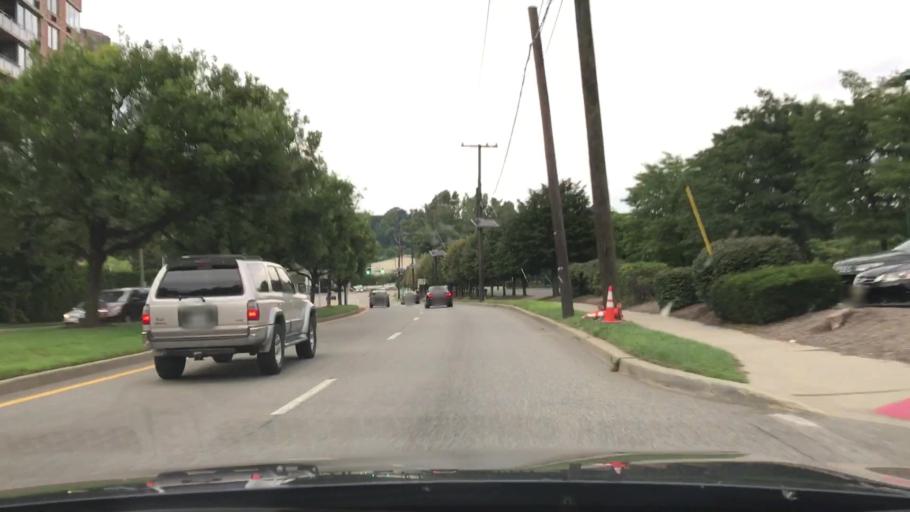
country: US
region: New Jersey
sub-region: Bergen County
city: Fairview
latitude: 40.8078
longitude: -73.9901
